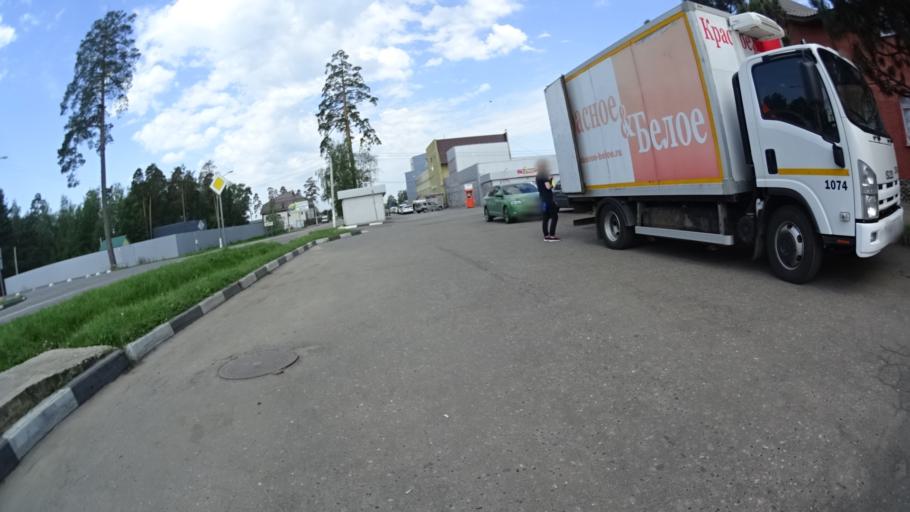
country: RU
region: Moskovskaya
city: Lesnoy
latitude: 56.0820
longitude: 37.9242
